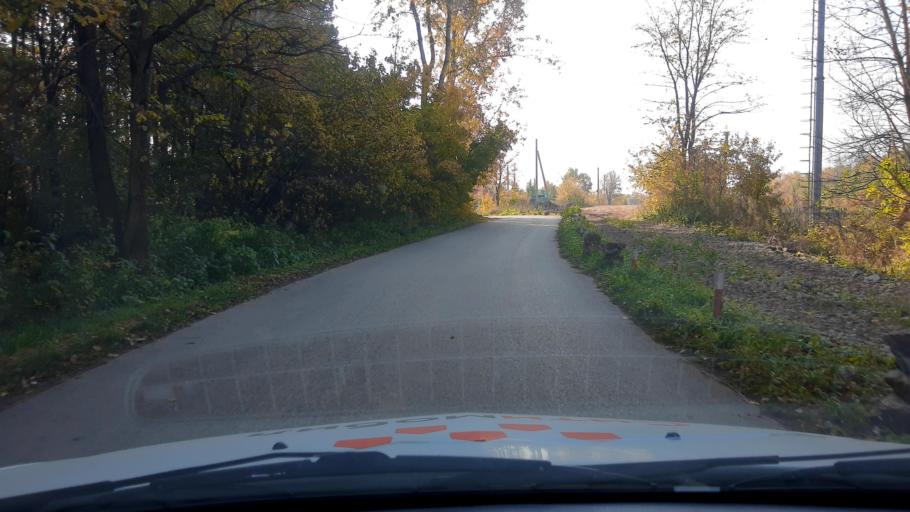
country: RU
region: Bashkortostan
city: Ufa
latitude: 54.6606
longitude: 56.0609
